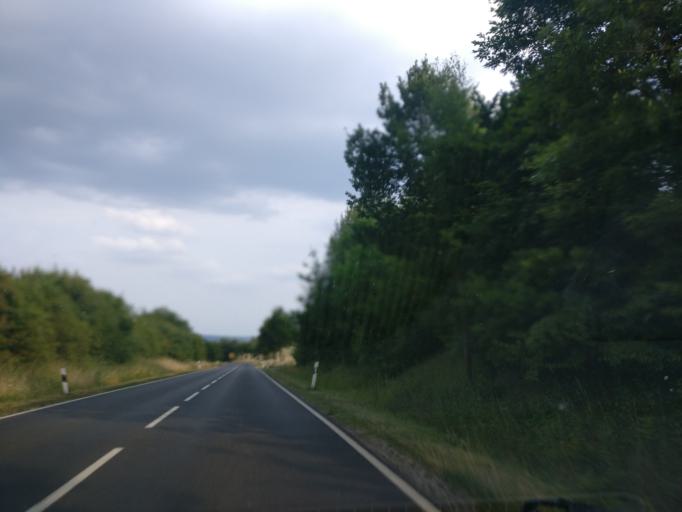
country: DE
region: Lower Saxony
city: Bovenden
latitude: 51.5813
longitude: 9.8683
